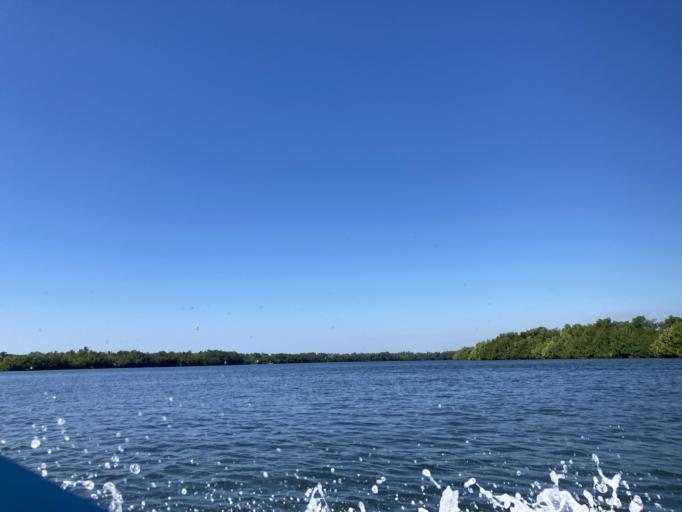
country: GT
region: Jutiapa
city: Pasaco
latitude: 13.8110
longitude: -90.2782
